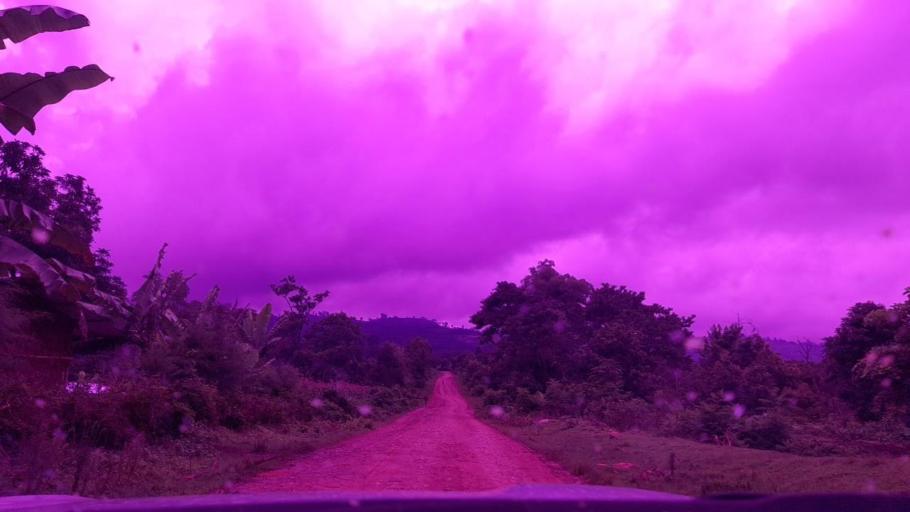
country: ET
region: Southern Nations, Nationalities, and People's Region
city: Bonga
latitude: 7.5552
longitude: 35.8400
